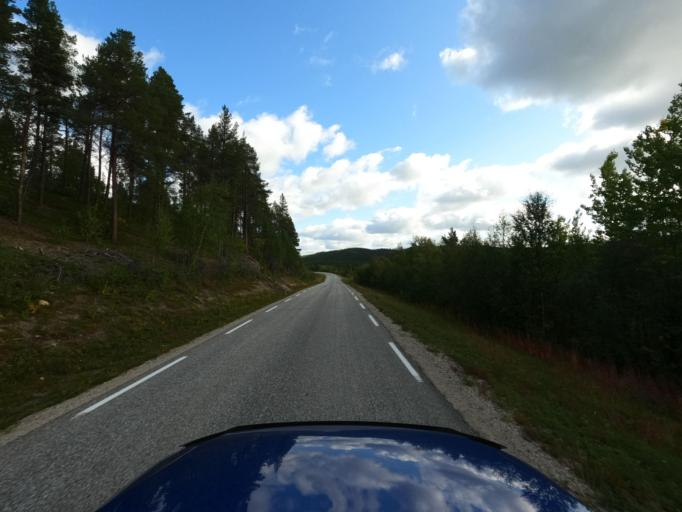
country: NO
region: Finnmark Fylke
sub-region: Karasjok
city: Karasjohka
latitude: 69.4330
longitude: 25.1423
